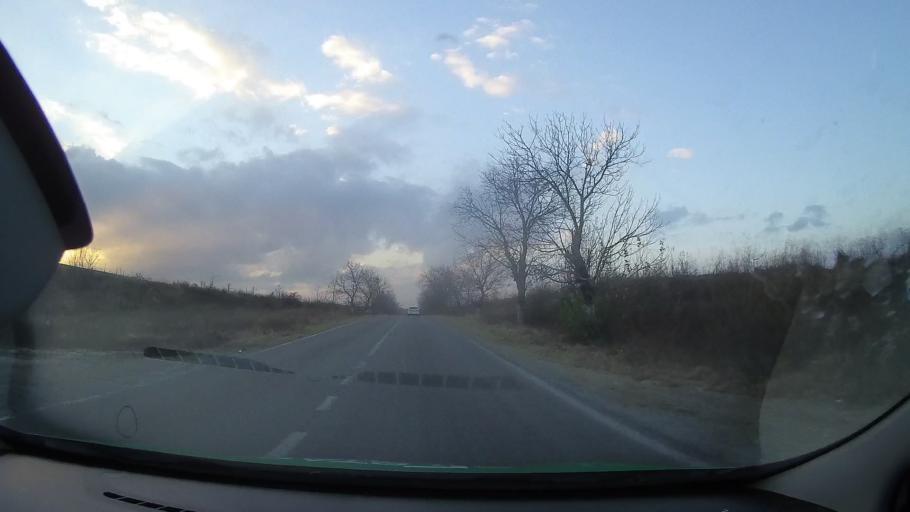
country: RO
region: Constanta
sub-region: Comuna Lipnita
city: Lipnita
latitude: 44.0946
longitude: 27.6405
